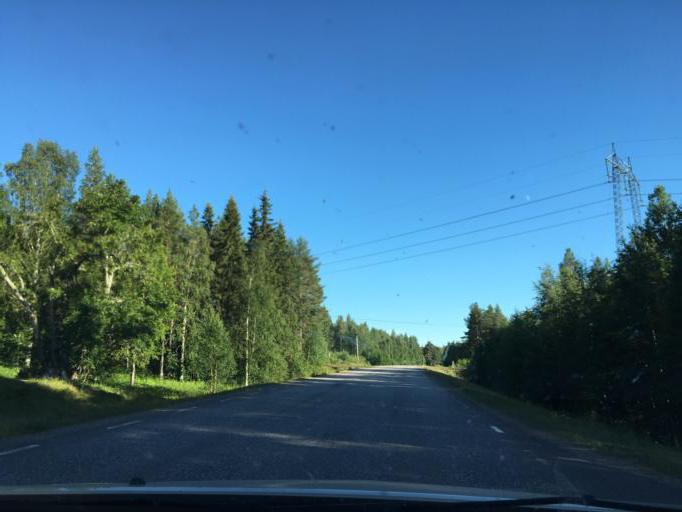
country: SE
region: Norrbotten
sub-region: Kalix Kommun
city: Rolfs
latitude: 65.9106
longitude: 22.9282
